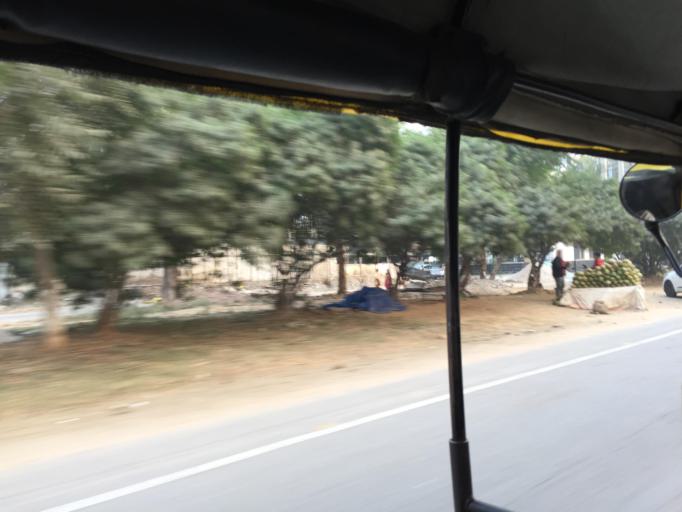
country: IN
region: Haryana
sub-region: Gurgaon
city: Gurgaon
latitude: 28.4253
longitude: 77.1052
